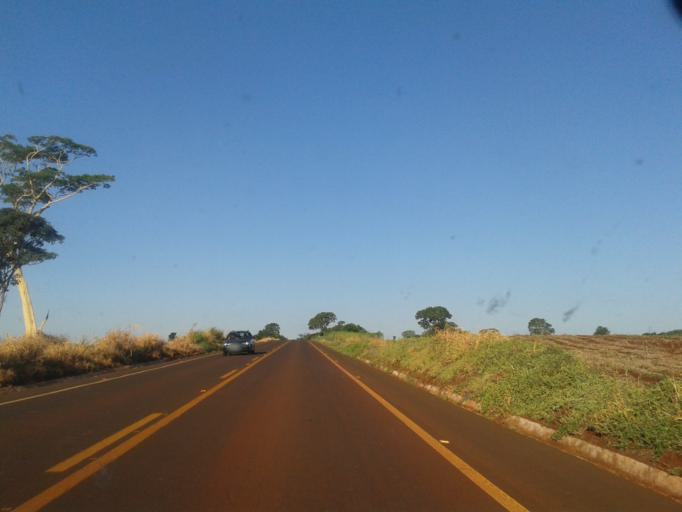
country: BR
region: Minas Gerais
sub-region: Capinopolis
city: Capinopolis
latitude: -18.7120
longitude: -49.7968
